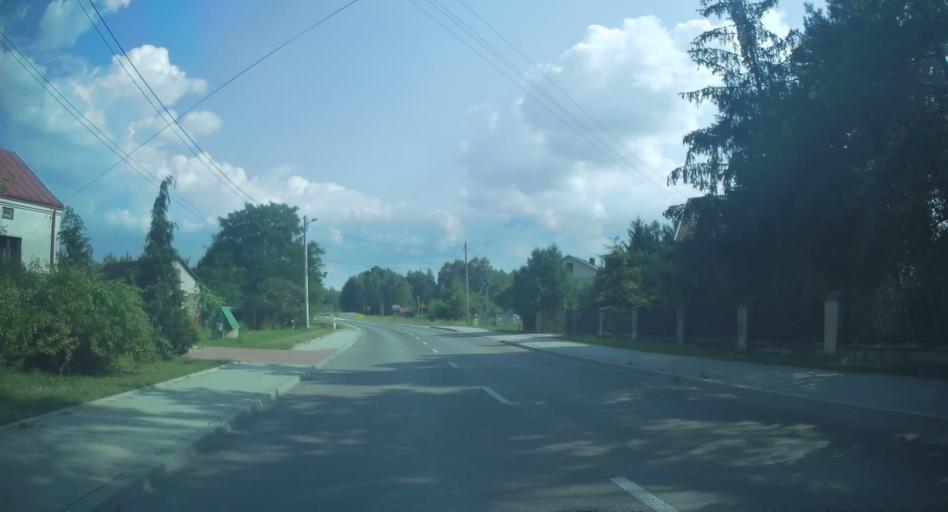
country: PL
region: Swietokrzyskie
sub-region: Powiat konecki
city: Radoszyce
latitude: 51.0623
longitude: 20.2752
